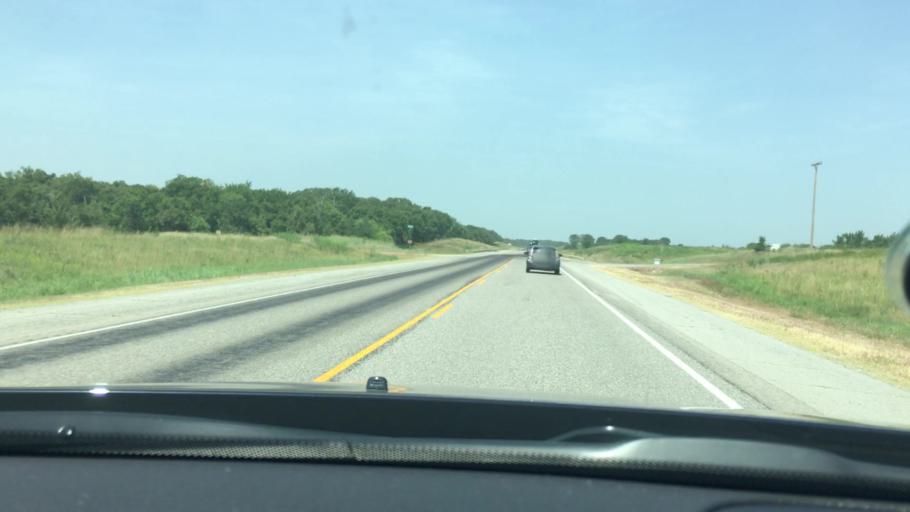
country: US
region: Oklahoma
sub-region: Coal County
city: Coalgate
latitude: 34.6002
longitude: -96.3443
